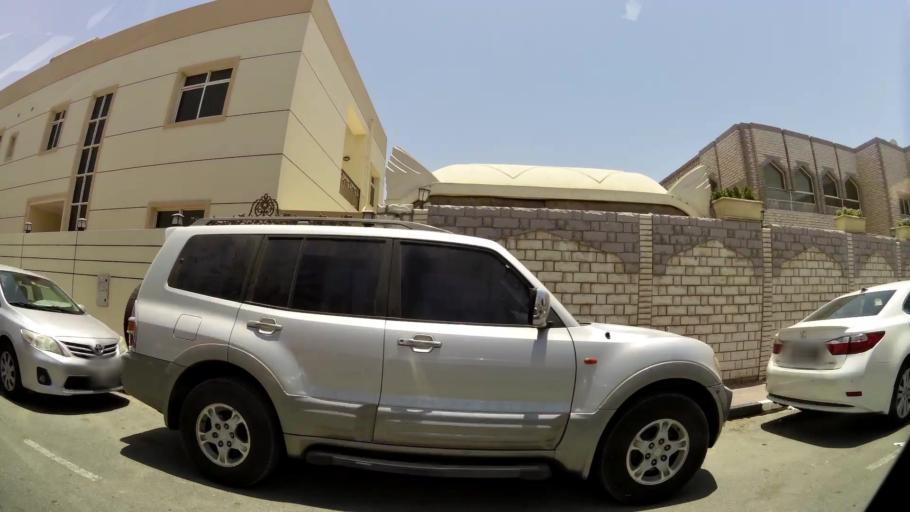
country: AE
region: Ash Shariqah
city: Sharjah
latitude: 25.2426
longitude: 55.2844
